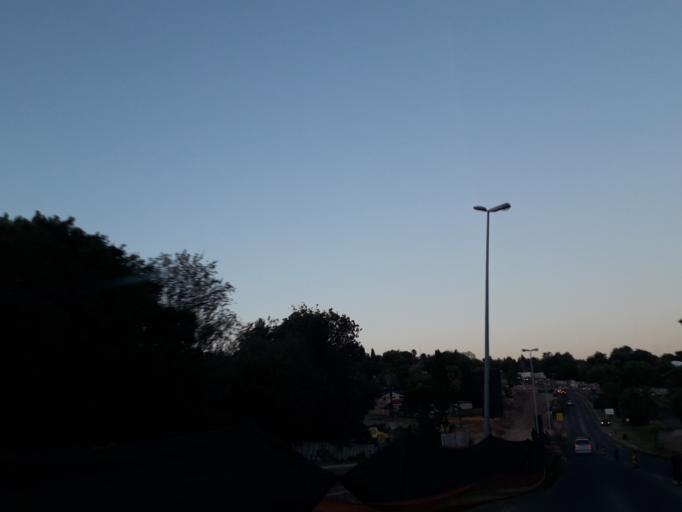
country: ZA
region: Gauteng
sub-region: City of Johannesburg Metropolitan Municipality
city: Roodepoort
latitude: -26.1216
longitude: 27.9322
